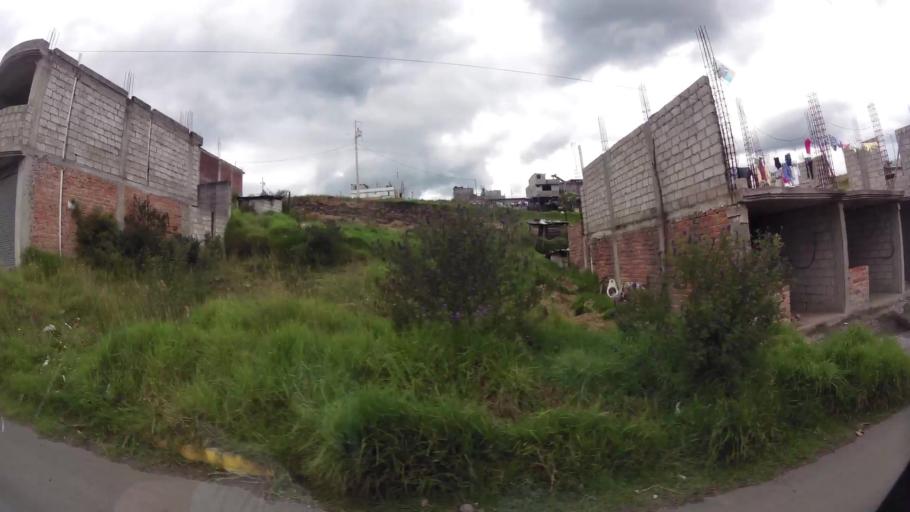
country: EC
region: Pichincha
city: Sangolqui
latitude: -0.3271
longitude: -78.5228
